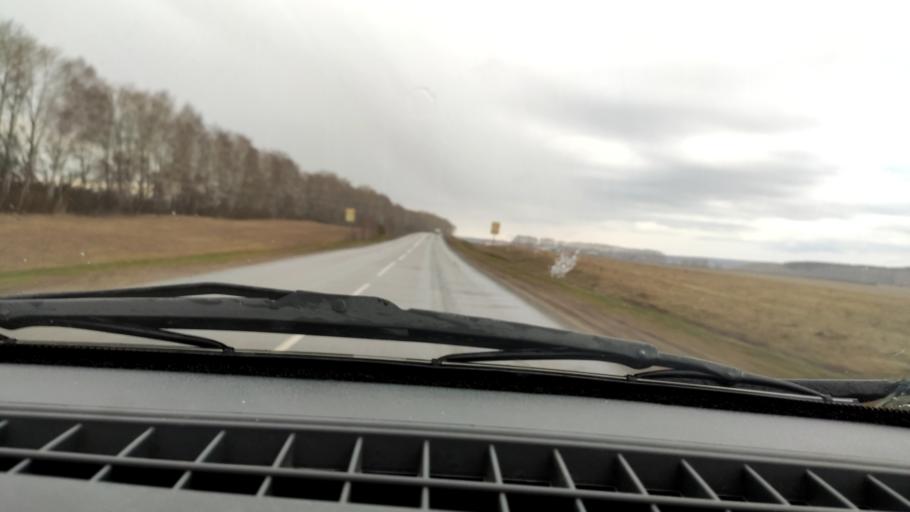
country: RU
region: Bashkortostan
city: Chekmagush
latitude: 55.1269
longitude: 54.7005
